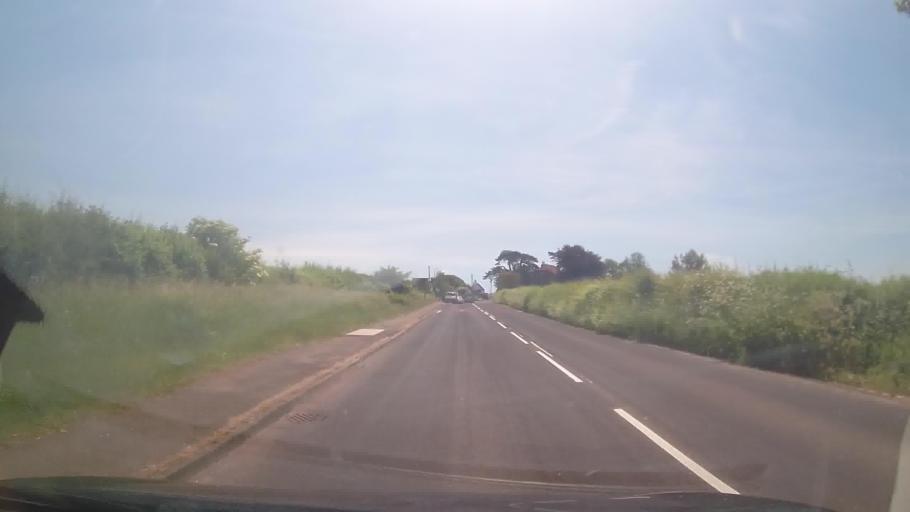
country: GB
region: Wales
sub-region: Monmouthshire
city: Monmouth
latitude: 51.8291
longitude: -2.7140
